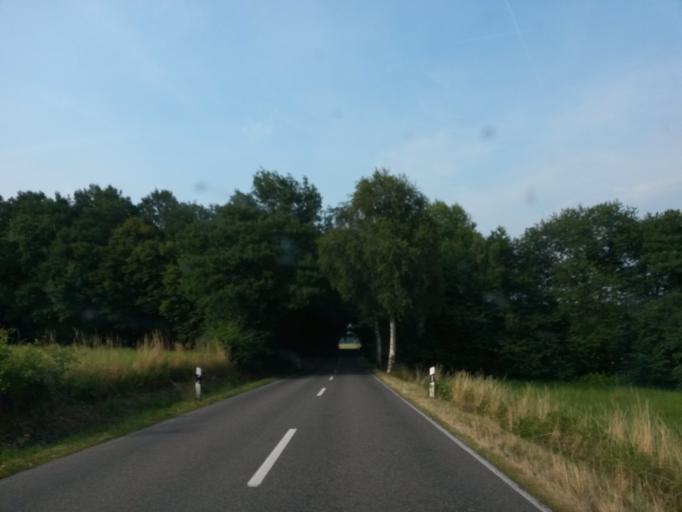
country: DE
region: North Rhine-Westphalia
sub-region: Regierungsbezirk Koln
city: Much
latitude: 50.8766
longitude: 7.4002
